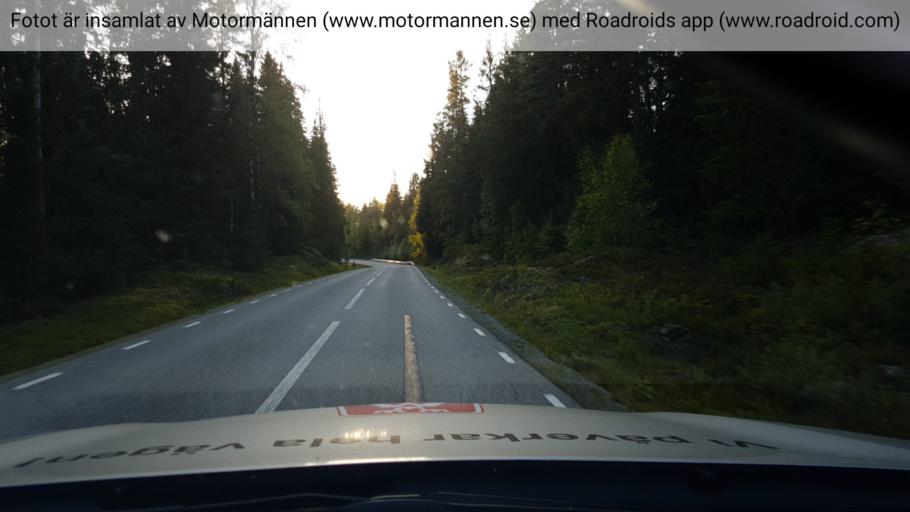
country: SE
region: OErebro
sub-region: Lindesbergs Kommun
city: Stora
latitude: 59.8942
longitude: 15.2781
